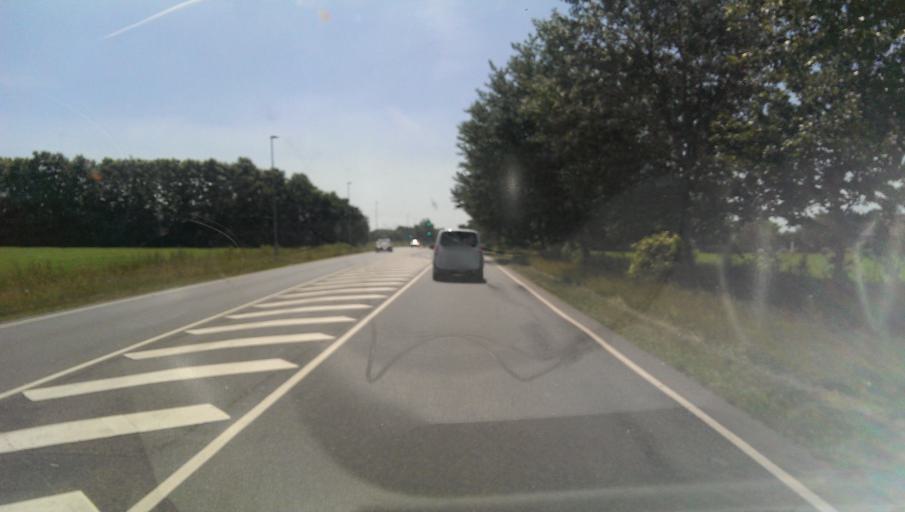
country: DK
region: South Denmark
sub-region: Esbjerg Kommune
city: Esbjerg
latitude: 55.5313
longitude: 8.4133
